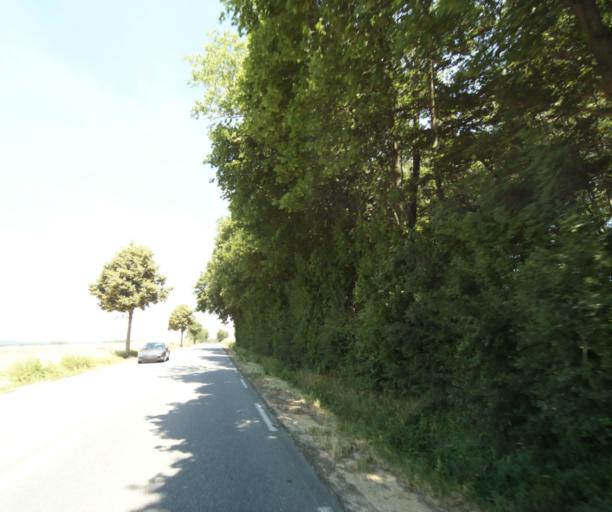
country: FR
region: Lorraine
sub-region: Departement de Meurthe-et-Moselle
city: Luneville
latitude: 48.6153
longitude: 6.4875
